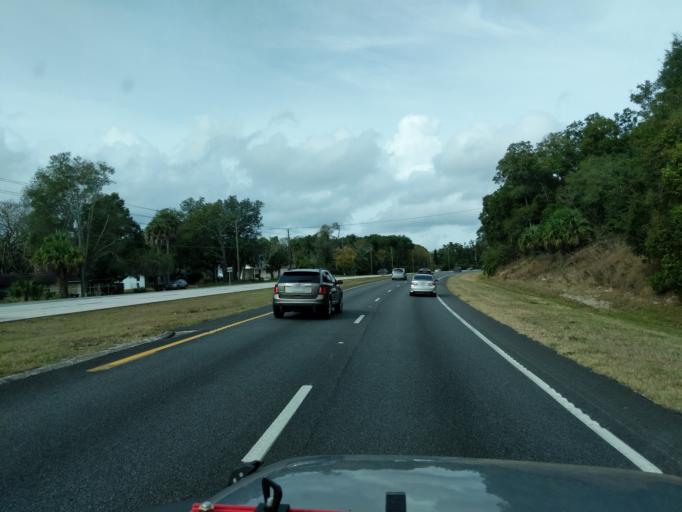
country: US
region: Florida
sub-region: Orange County
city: Zellwood
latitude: 28.7372
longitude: -81.6140
